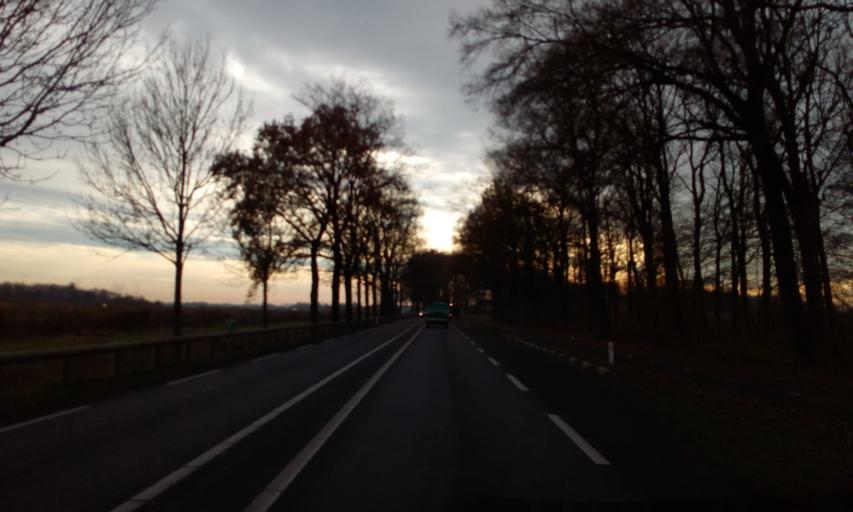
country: NL
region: South Holland
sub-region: Gemeente Rijnwoude
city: Benthuizen
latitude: 52.0650
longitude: 4.5594
